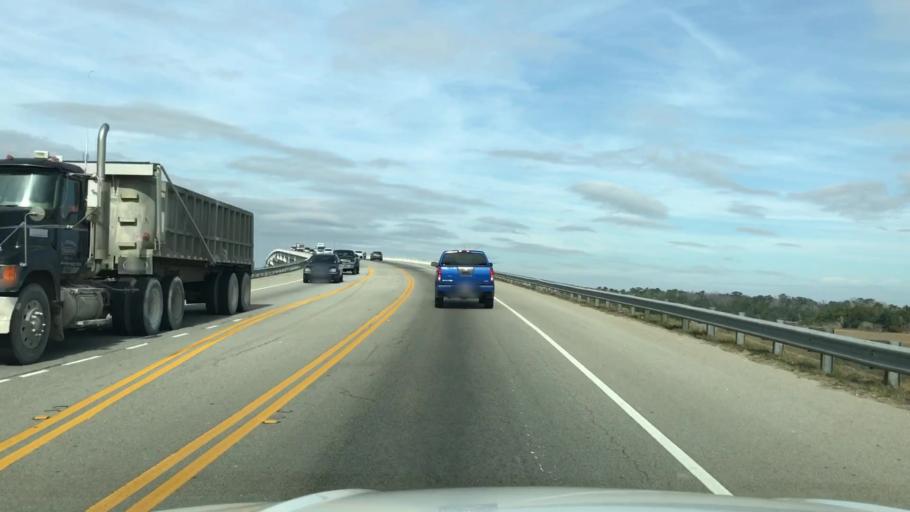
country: US
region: South Carolina
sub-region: Charleston County
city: Shell Point
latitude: 32.7809
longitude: -80.1059
